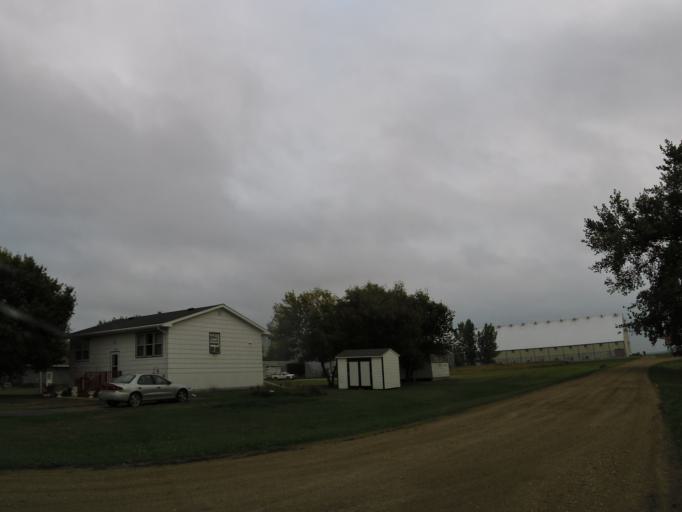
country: US
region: North Dakota
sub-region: Walsh County
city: Grafton
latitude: 48.5568
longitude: -97.1820
